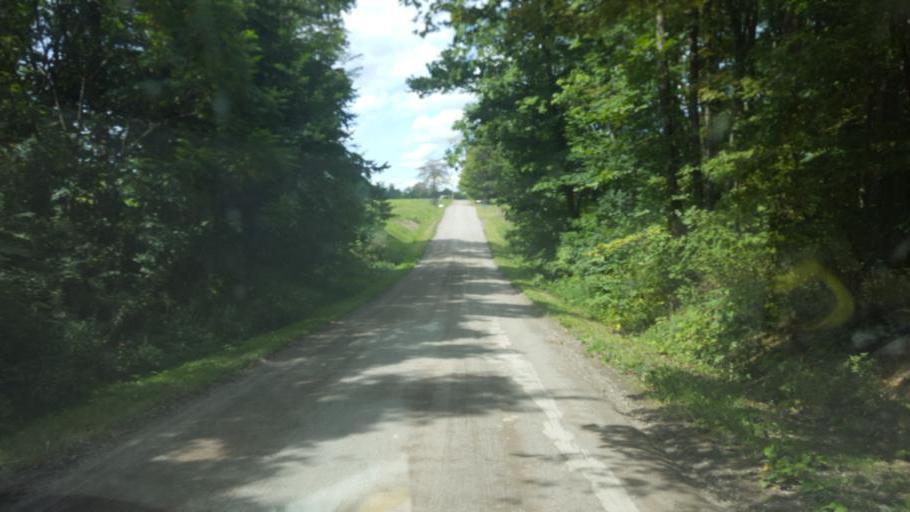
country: US
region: Ohio
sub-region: Geauga County
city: Middlefield
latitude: 41.4258
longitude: -80.9857
